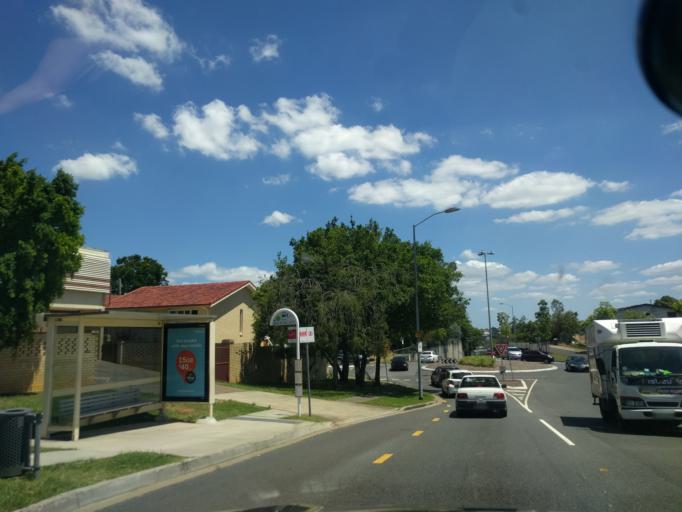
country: AU
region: Queensland
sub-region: Brisbane
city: Stafford Heights
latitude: -27.4004
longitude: 153.0096
